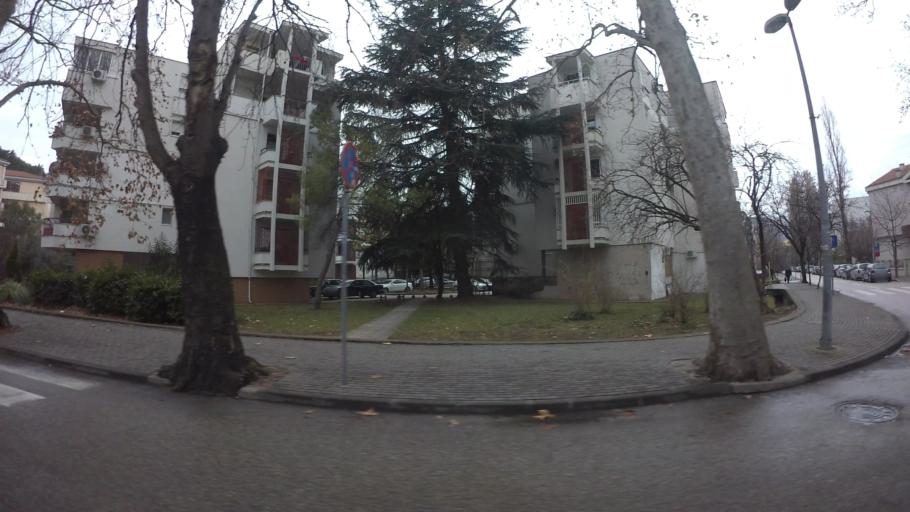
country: BA
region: Federation of Bosnia and Herzegovina
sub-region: Hercegovacko-Bosanski Kanton
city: Mostar
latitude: 43.3405
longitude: 17.7998
